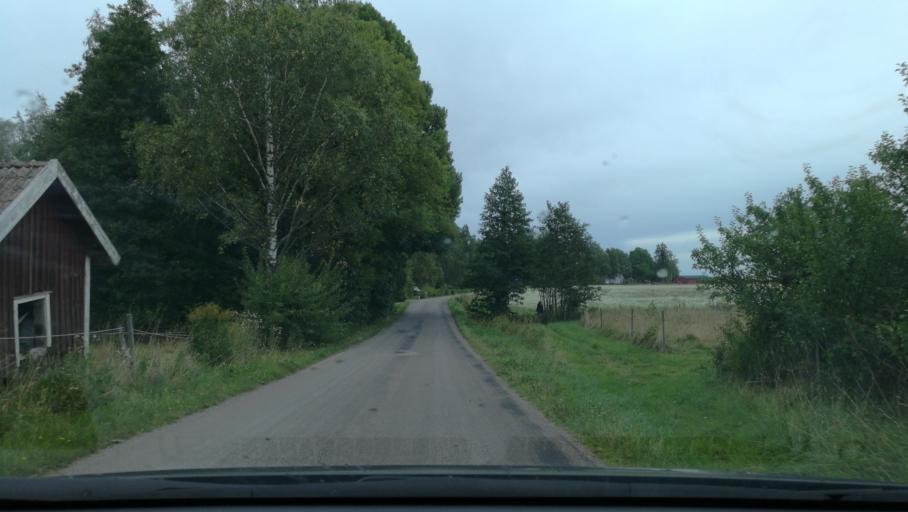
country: SE
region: Vaestmanland
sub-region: Vasteras
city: Tillberga
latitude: 59.7156
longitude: 16.5886
